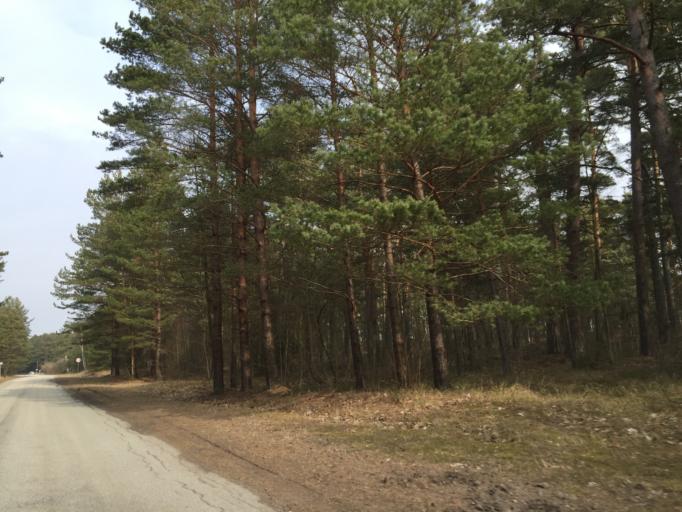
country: LV
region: Salacgrivas
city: Ainazi
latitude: 57.9242
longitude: 24.3902
